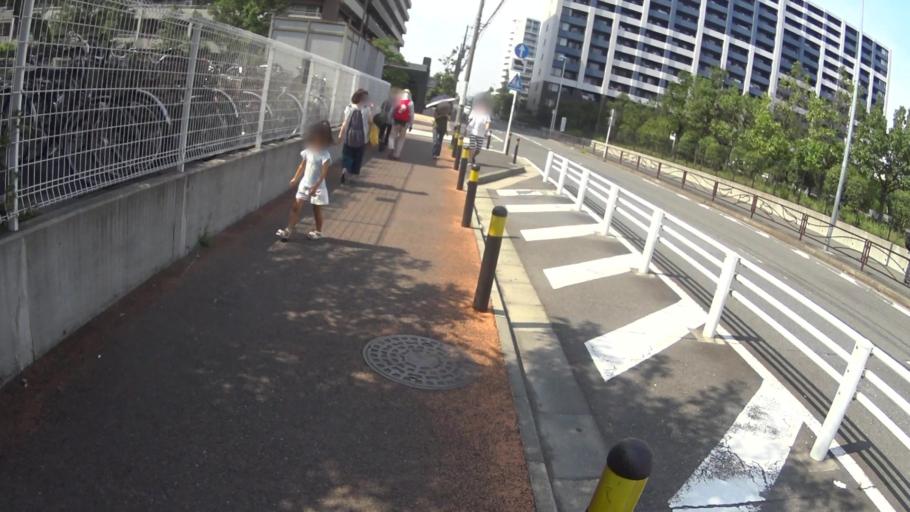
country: JP
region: Kanagawa
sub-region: Kawasaki-shi
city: Kawasaki
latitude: 35.5380
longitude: 139.7350
